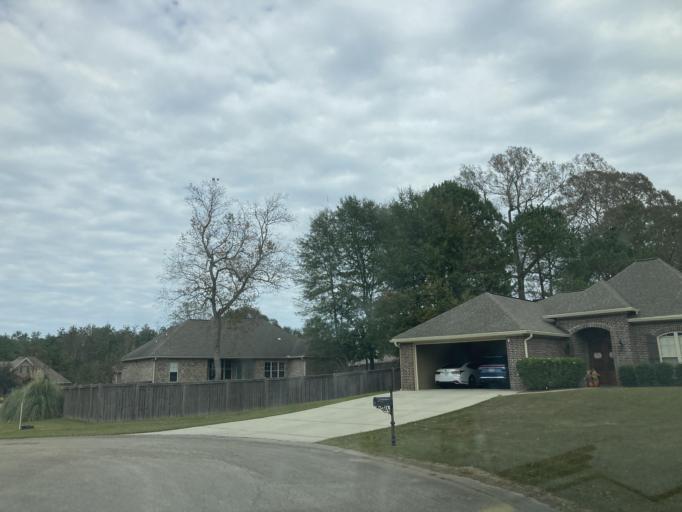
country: US
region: Mississippi
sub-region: Lamar County
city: West Hattiesburg
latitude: 31.2918
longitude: -89.4448
